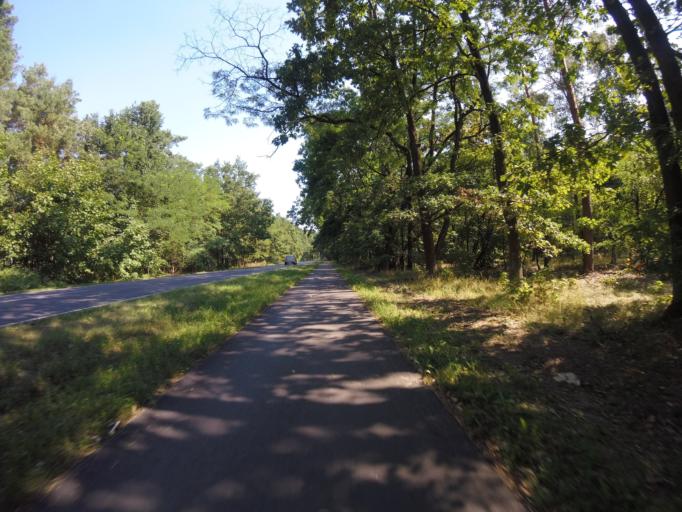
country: DE
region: Brandenburg
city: Mullrose
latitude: 52.2658
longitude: 14.4346
